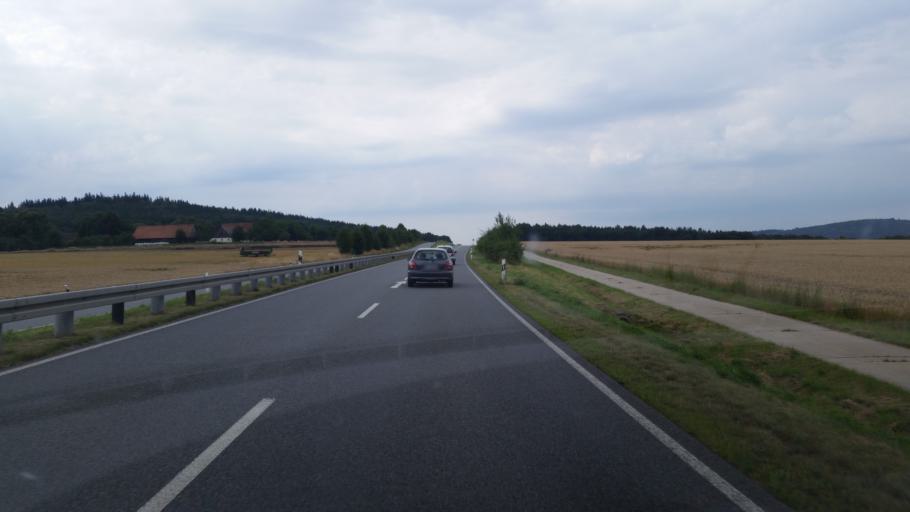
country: DE
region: Saxony
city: Elstra
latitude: 51.2142
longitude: 14.1535
